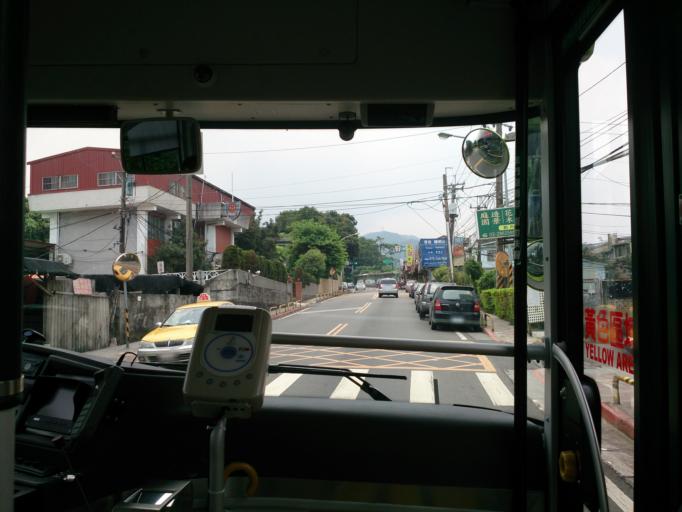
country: TW
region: Taipei
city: Taipei
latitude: 25.1180
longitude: 121.5522
